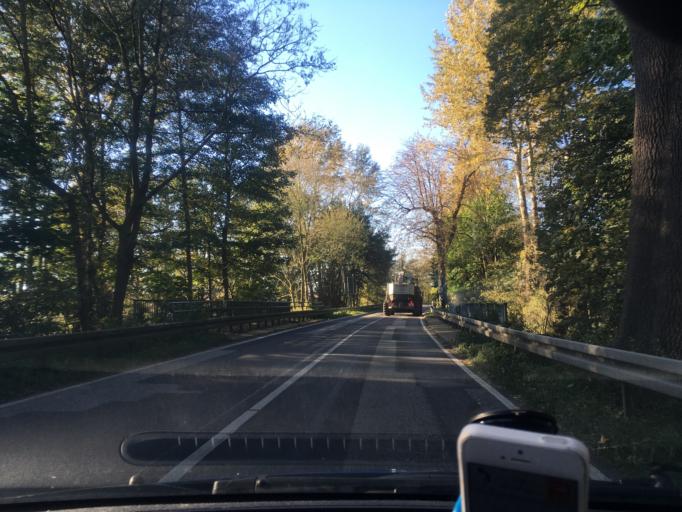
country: DE
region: Mecklenburg-Vorpommern
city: Zarrentin
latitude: 53.5328
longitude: 10.9462
